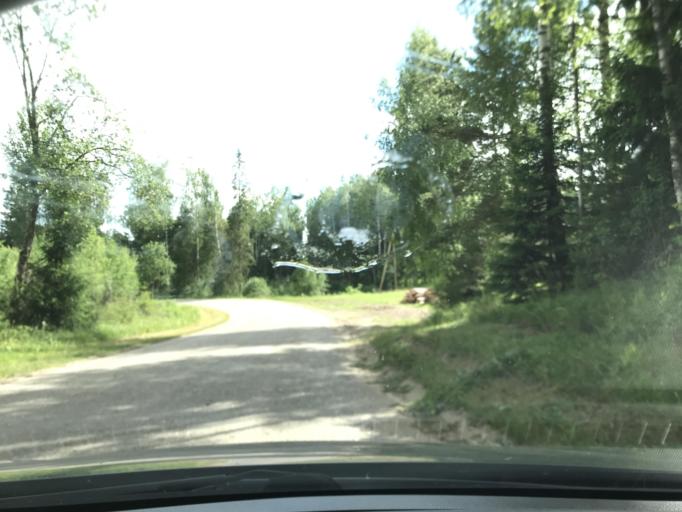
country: LV
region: Alsunga
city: Alsunga
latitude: 56.9853
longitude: 21.6303
